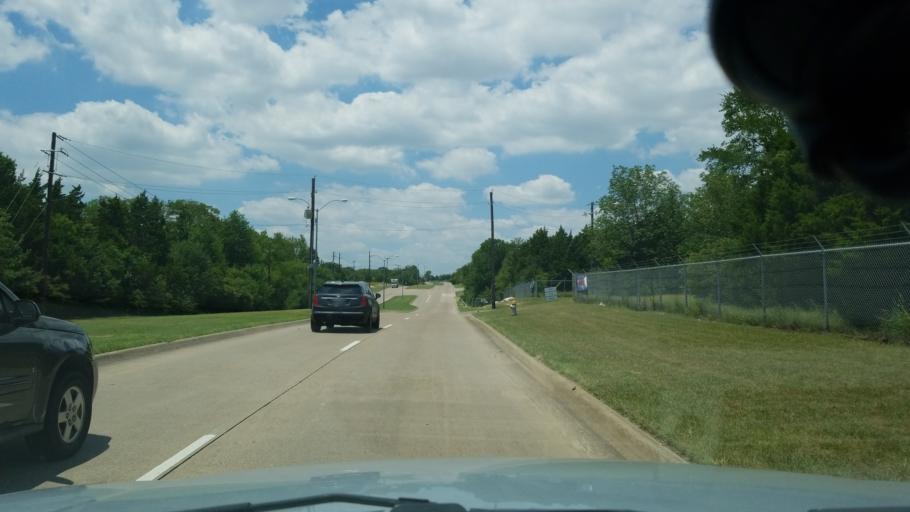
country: US
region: Texas
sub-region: Dallas County
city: Duncanville
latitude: 32.6720
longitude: -96.8724
